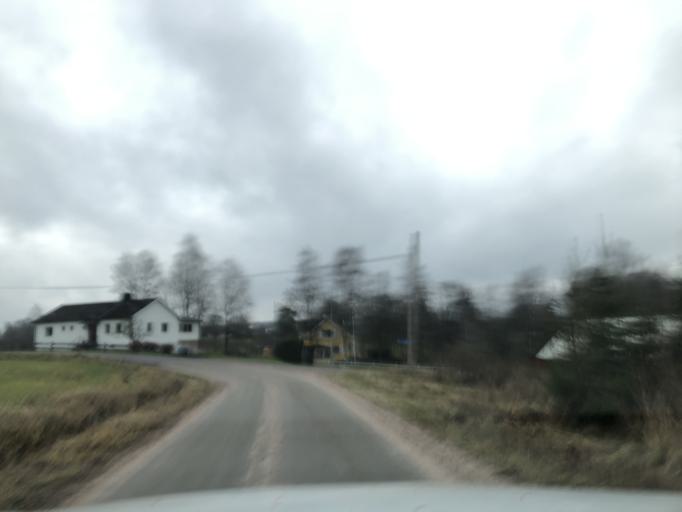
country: SE
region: Vaestra Goetaland
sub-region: Ulricehamns Kommun
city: Ulricehamn
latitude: 57.8653
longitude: 13.5540
